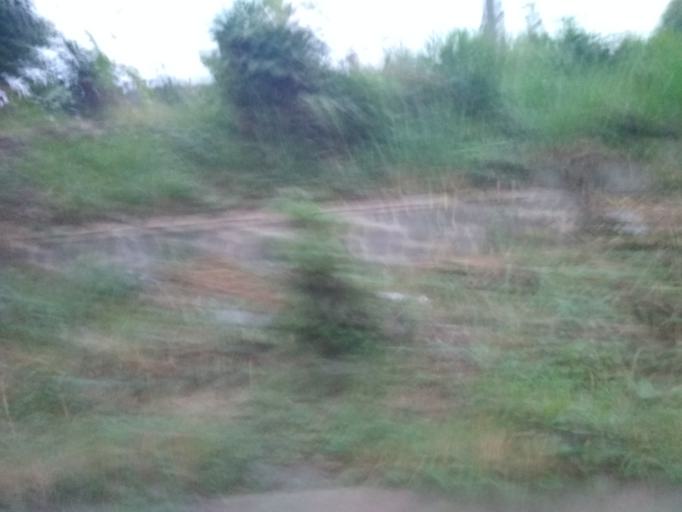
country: ID
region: West Java
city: Caringin
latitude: -6.7192
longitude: 106.8200
